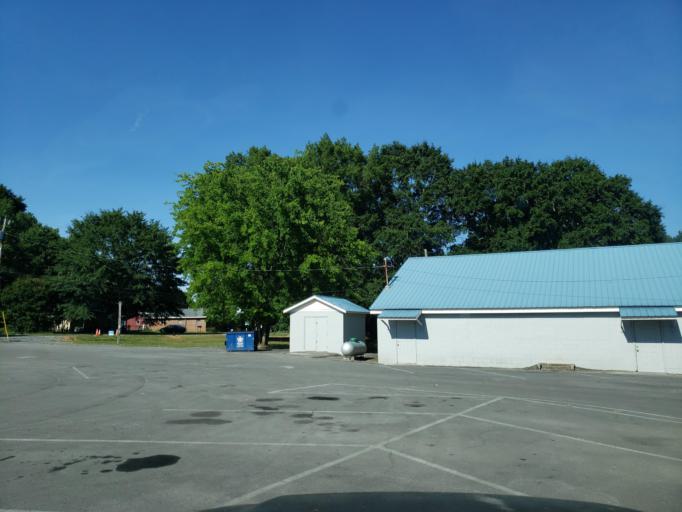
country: US
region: Georgia
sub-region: Gordon County
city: Calhoun
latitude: 34.5791
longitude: -84.9468
